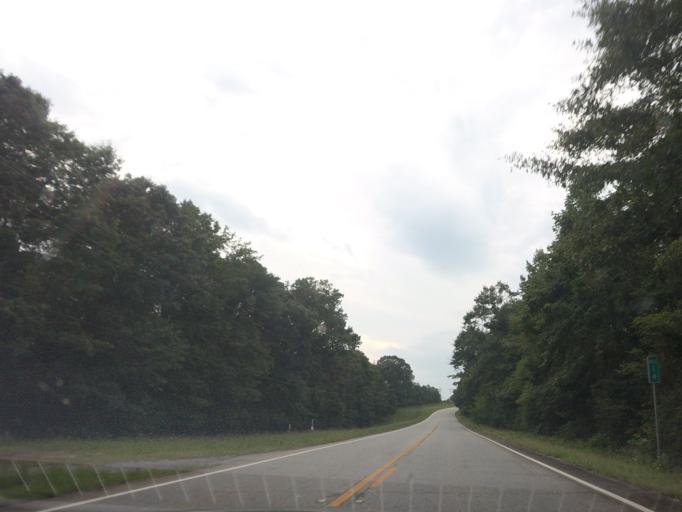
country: US
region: Georgia
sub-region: Twiggs County
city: Jeffersonville
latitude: 32.7188
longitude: -83.4080
